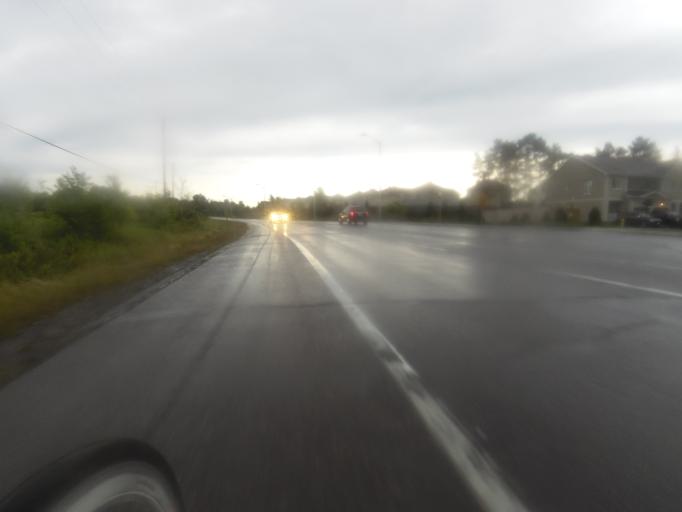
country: CA
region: Ontario
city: Bells Corners
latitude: 45.2530
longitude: -75.7254
